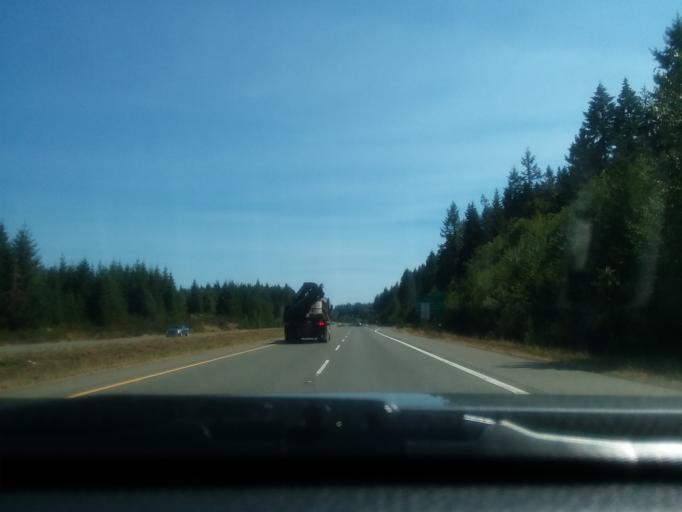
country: CA
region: British Columbia
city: Port Alberni
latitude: 49.4364
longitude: -124.7509
